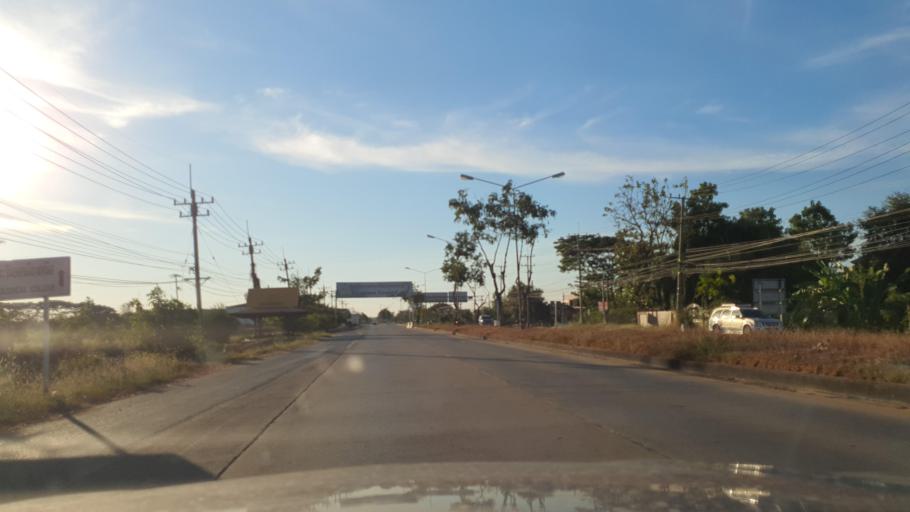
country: TH
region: Khon Kaen
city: Khon Kaen
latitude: 16.4375
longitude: 102.9146
